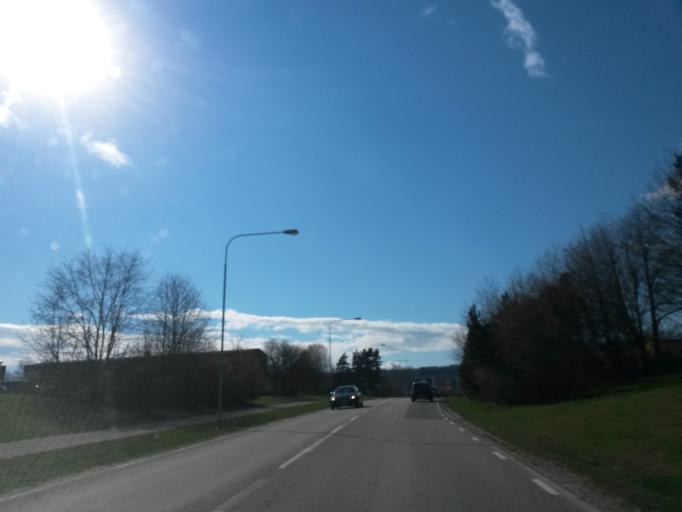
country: SE
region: Vaestra Goetaland
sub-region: Skovde Kommun
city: Skoevde
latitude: 58.4067
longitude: 13.8629
